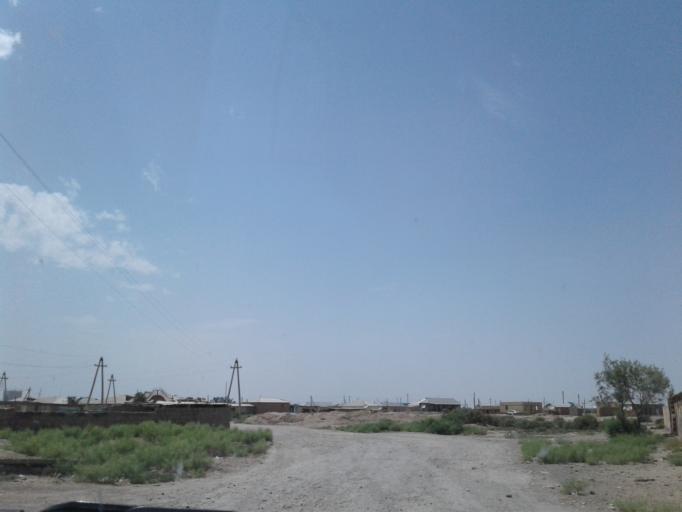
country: IR
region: Razavi Khorasan
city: Kalat-e Naderi
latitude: 37.2002
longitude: 60.0273
